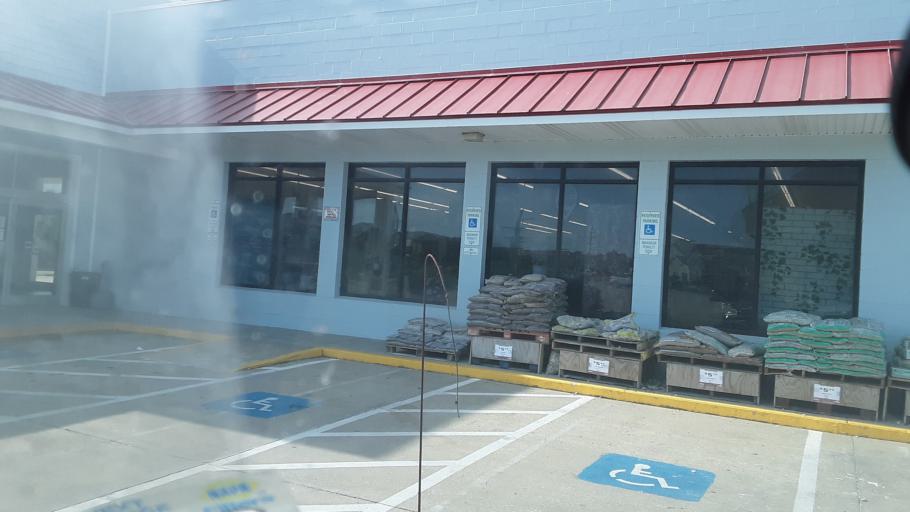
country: US
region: North Carolina
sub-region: Dare County
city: Buxton
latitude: 35.3319
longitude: -75.5080
